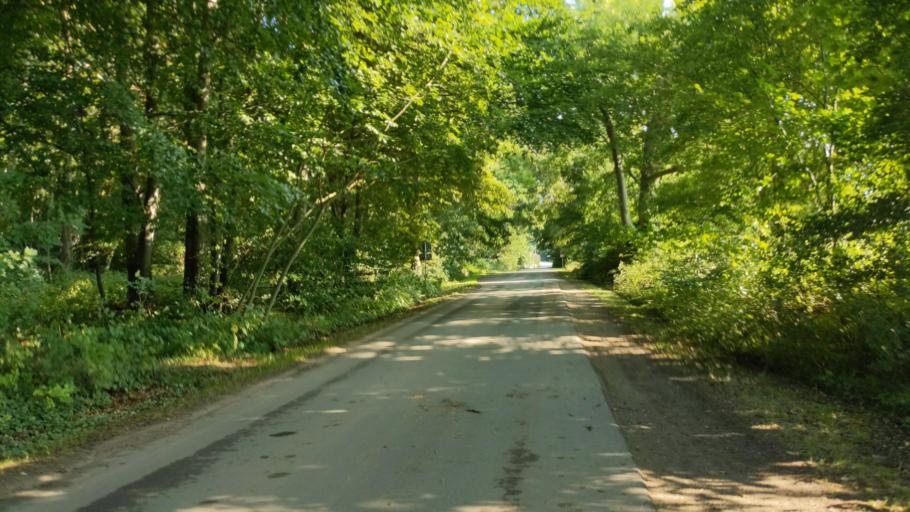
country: DE
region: Mecklenburg-Vorpommern
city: Kalkhorst
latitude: 54.0017
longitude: 11.0445
